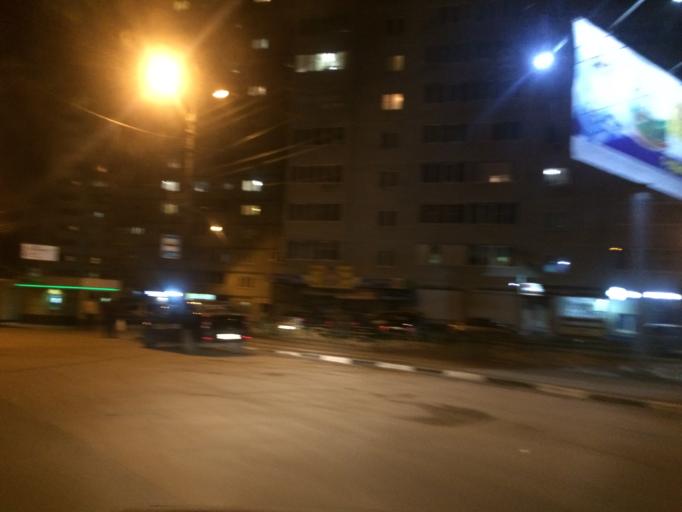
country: RU
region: Tula
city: Tula
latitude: 54.2093
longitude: 37.6934
